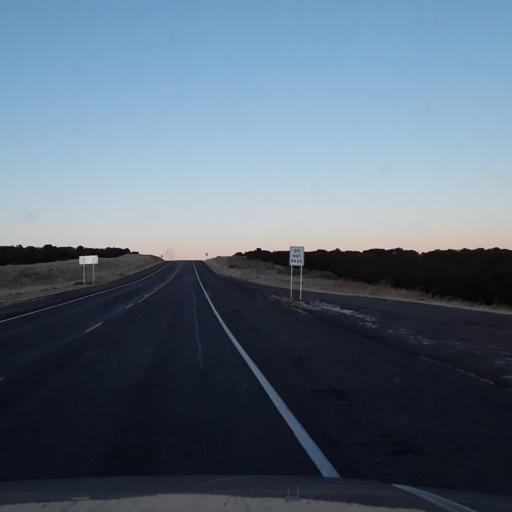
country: US
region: New Mexico
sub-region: Guadalupe County
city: Santa Rosa
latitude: 34.5294
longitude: -105.3223
